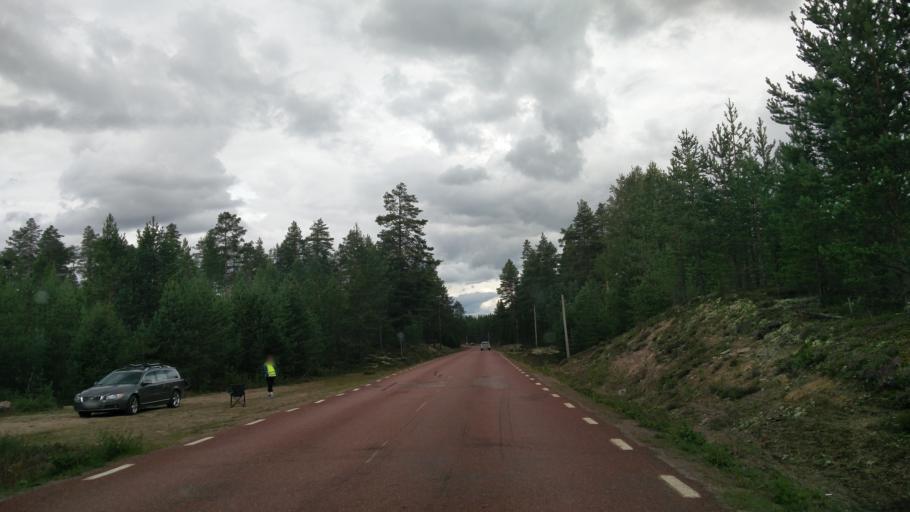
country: NO
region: Hedmark
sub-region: Trysil
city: Innbygda
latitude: 61.1395
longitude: 12.8073
